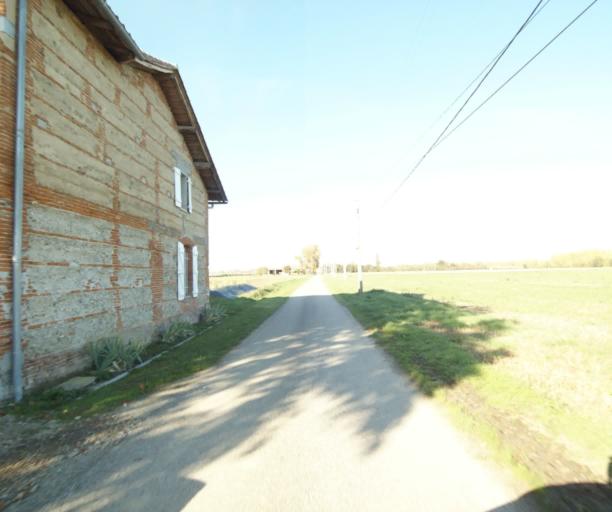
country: FR
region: Midi-Pyrenees
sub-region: Departement du Tarn-et-Garonne
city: Finhan
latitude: 43.9353
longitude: 1.2062
